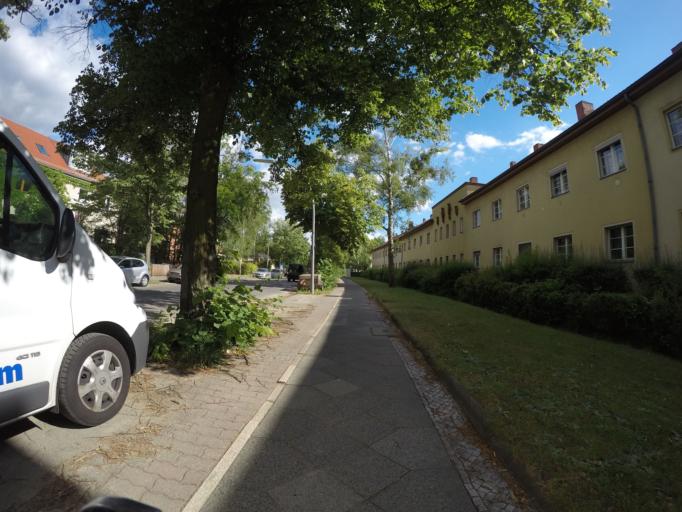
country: DE
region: Berlin
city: Zehlendorf Bezirk
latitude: 52.4395
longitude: 13.2705
